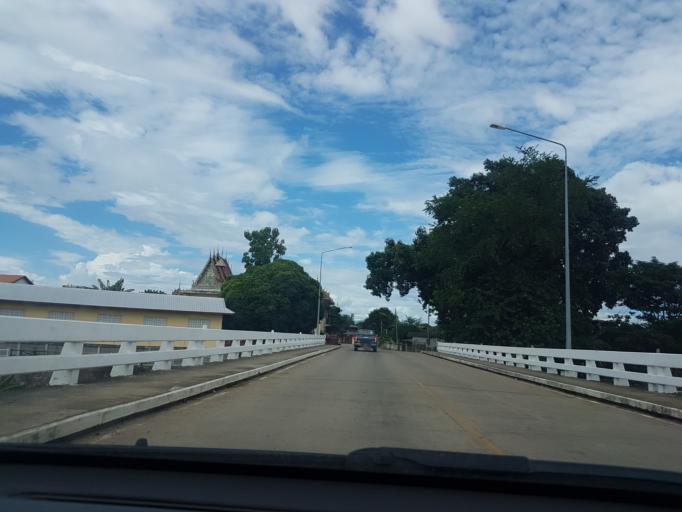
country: TH
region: Lampang
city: Ko Kha
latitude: 18.2342
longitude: 99.4220
